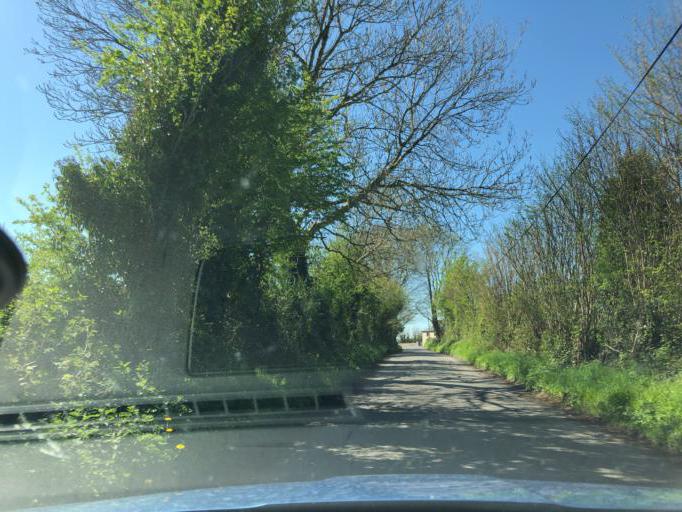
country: IE
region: Connaught
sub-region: County Galway
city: Portumna
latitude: 53.1501
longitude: -8.3386
